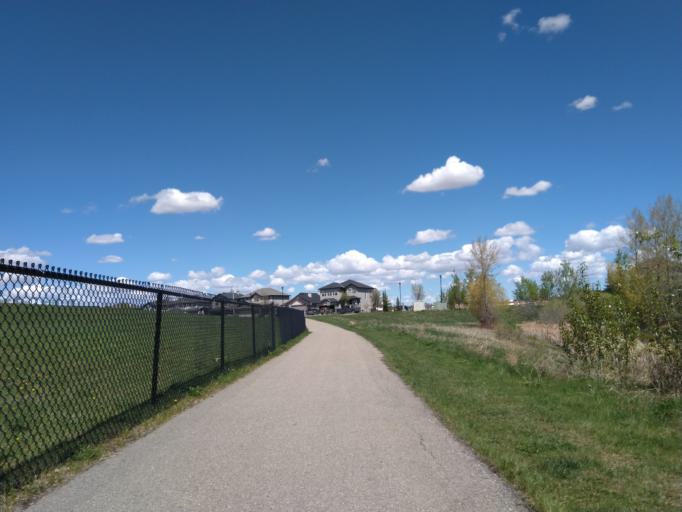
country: CA
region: Alberta
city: Chestermere
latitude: 51.0309
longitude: -113.8378
